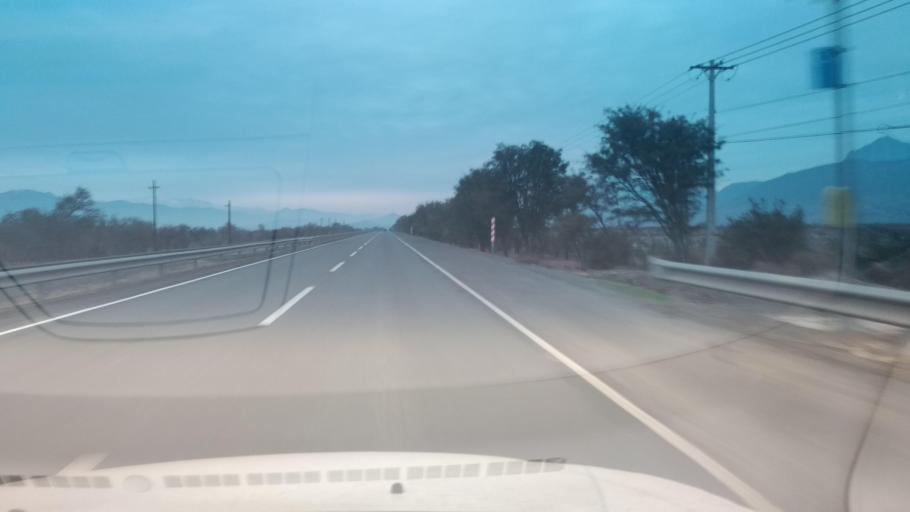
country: CL
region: Santiago Metropolitan
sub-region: Provincia de Chacabuco
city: Chicureo Abajo
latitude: -33.1007
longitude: -70.6914
